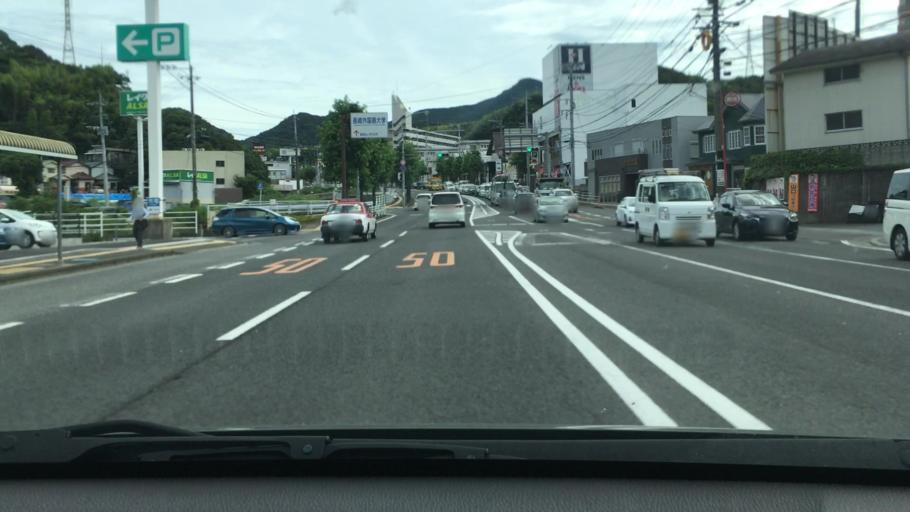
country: JP
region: Nagasaki
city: Togitsu
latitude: 32.8192
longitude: 129.8473
